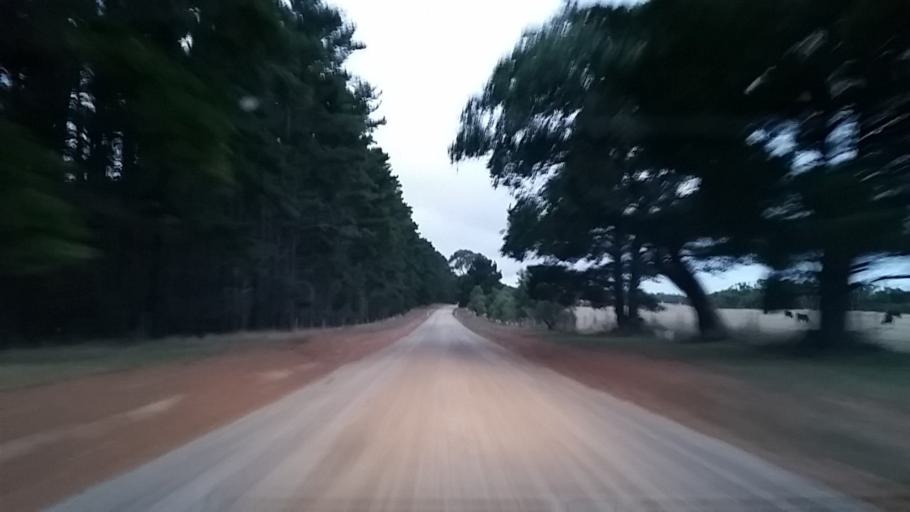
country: AU
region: South Australia
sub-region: Yankalilla
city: Normanville
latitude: -35.6099
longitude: 138.1867
